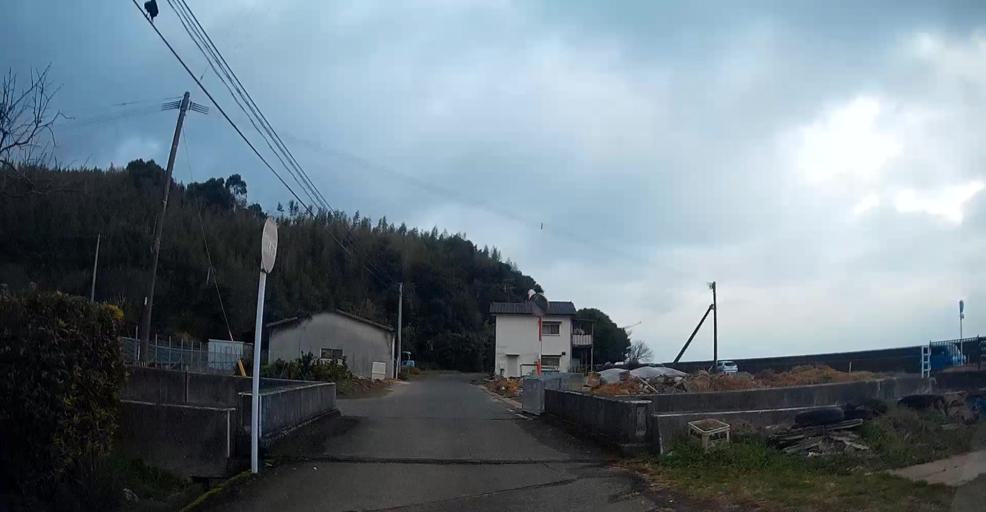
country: JP
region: Kumamoto
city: Matsubase
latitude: 32.6332
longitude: 130.6226
